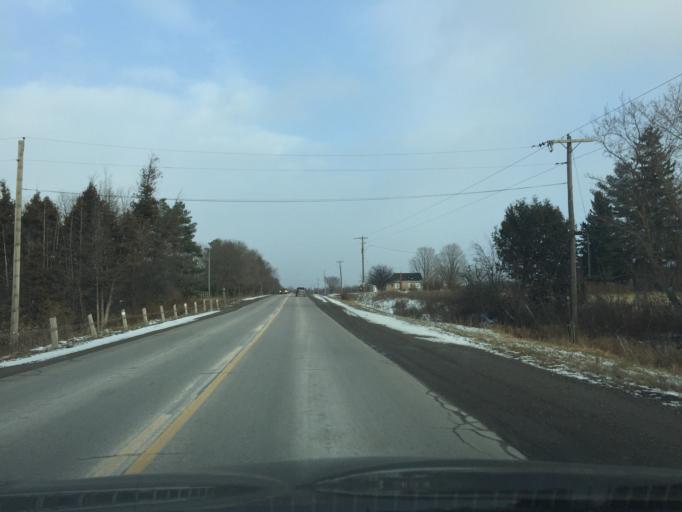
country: CA
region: Ontario
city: Uxbridge
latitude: 44.0704
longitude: -79.0170
